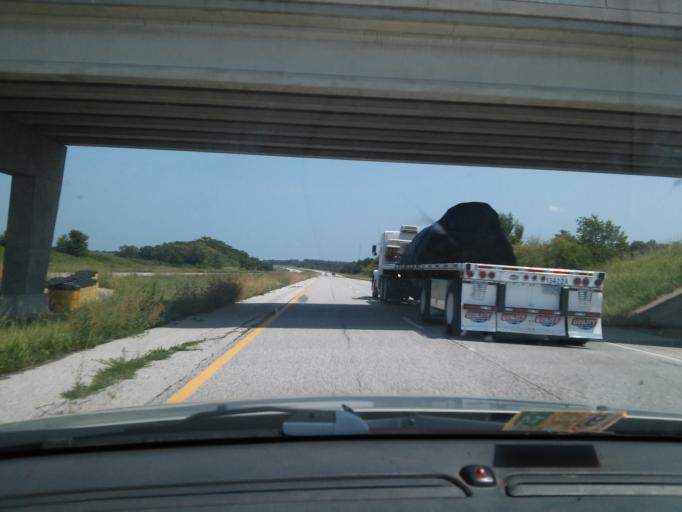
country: US
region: Illinois
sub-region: Pike County
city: Griggsville
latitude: 39.6782
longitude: -90.7038
